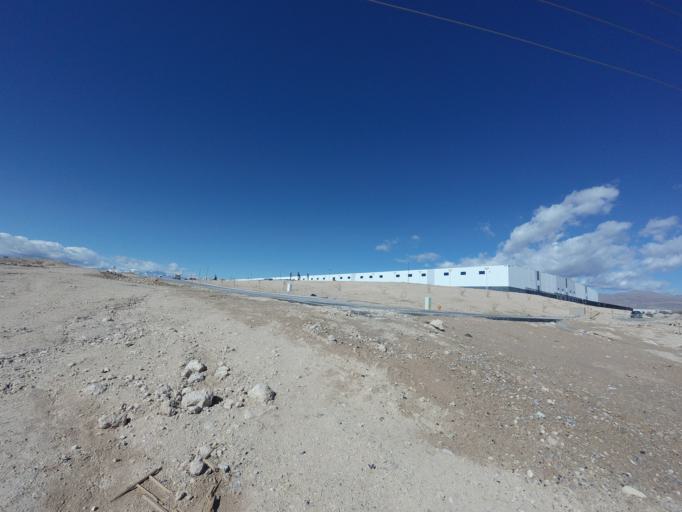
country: US
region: Nevada
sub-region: Clark County
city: Nellis Air Force Base
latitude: 36.2620
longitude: -115.0341
